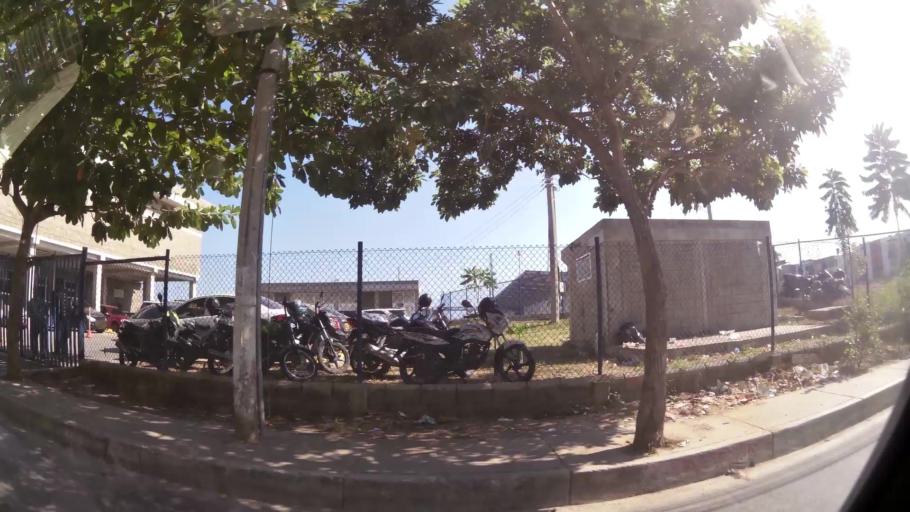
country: CO
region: Bolivar
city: Cartagena
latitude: 10.3945
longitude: -75.4740
